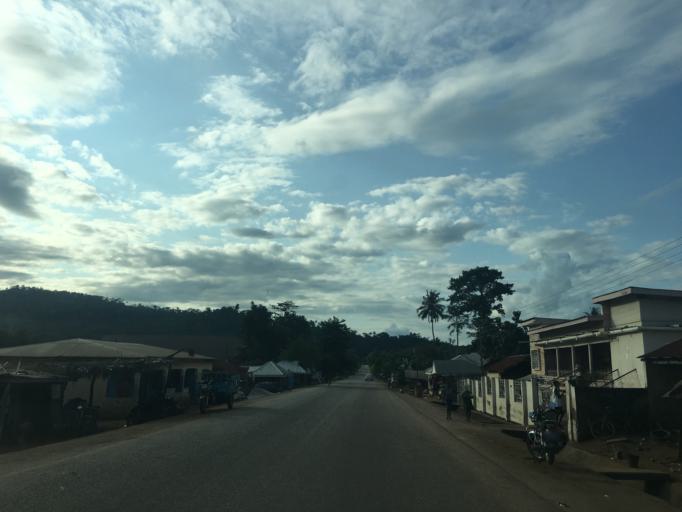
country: GH
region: Western
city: Bibiani
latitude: 6.2552
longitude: -2.2245
